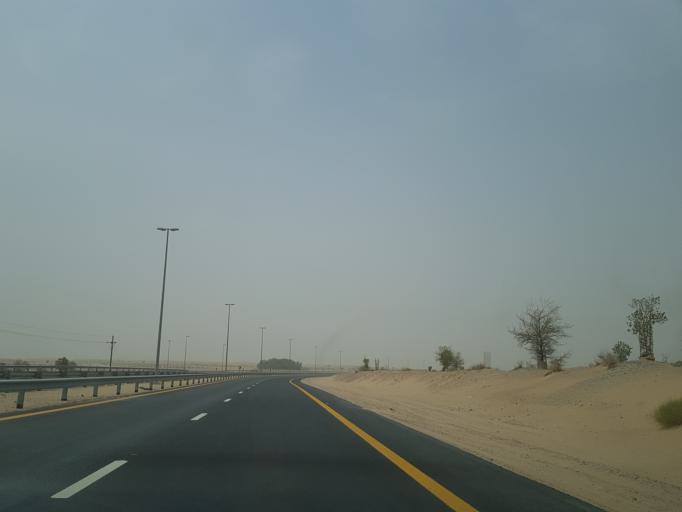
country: AE
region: Dubai
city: Dubai
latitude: 24.8787
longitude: 55.4211
